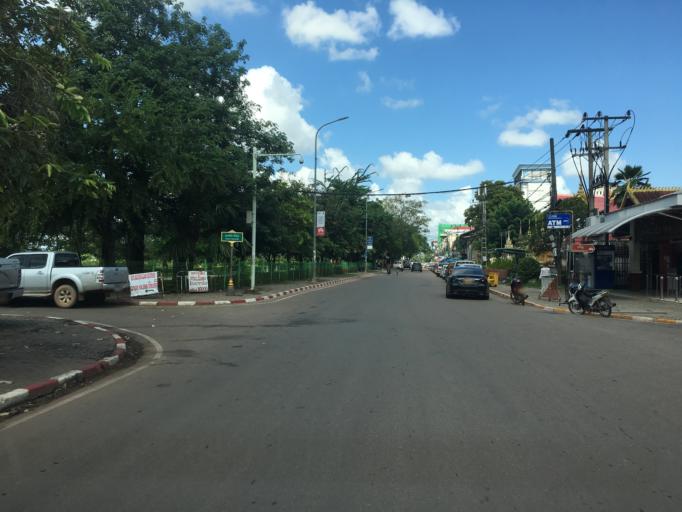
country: LA
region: Vientiane
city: Vientiane
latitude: 17.9627
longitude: 102.6069
